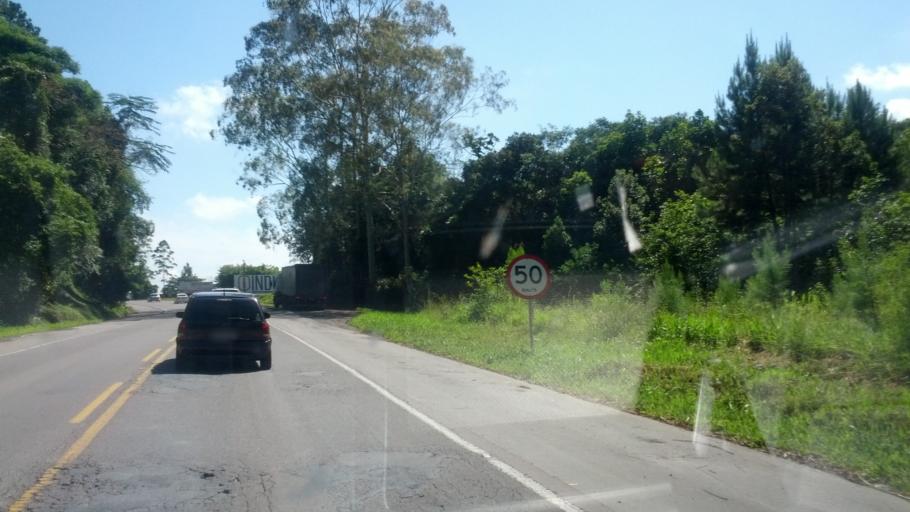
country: BR
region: Santa Catarina
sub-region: Rio Do Sul
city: Rio do Sul
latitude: -27.1676
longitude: -49.5599
